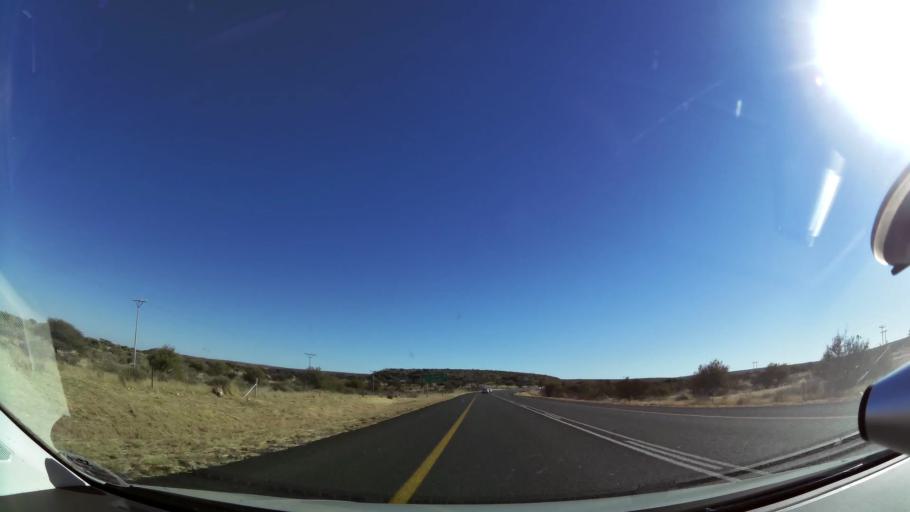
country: ZA
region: Northern Cape
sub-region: Frances Baard District Municipality
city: Warrenton
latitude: -28.3499
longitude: 24.8178
